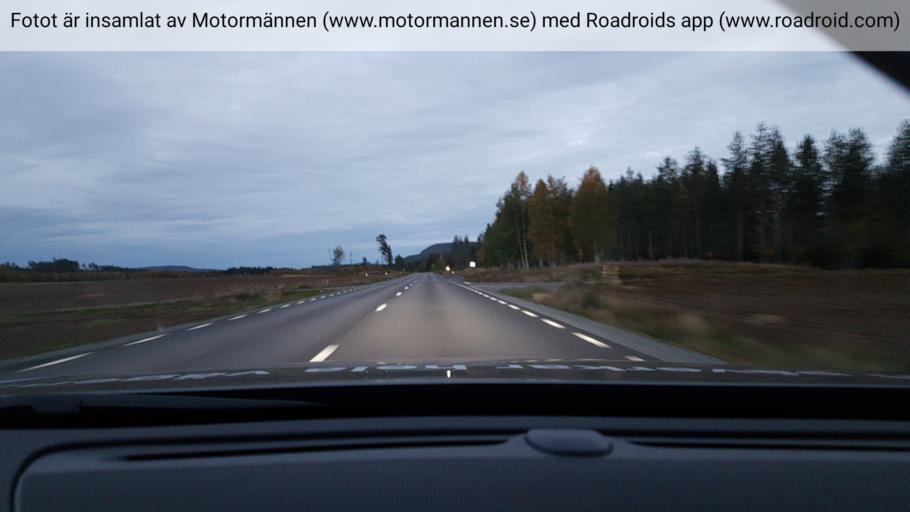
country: SE
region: Norrbotten
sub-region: Alvsbyns Kommun
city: AElvsbyn
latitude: 65.7650
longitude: 20.8711
